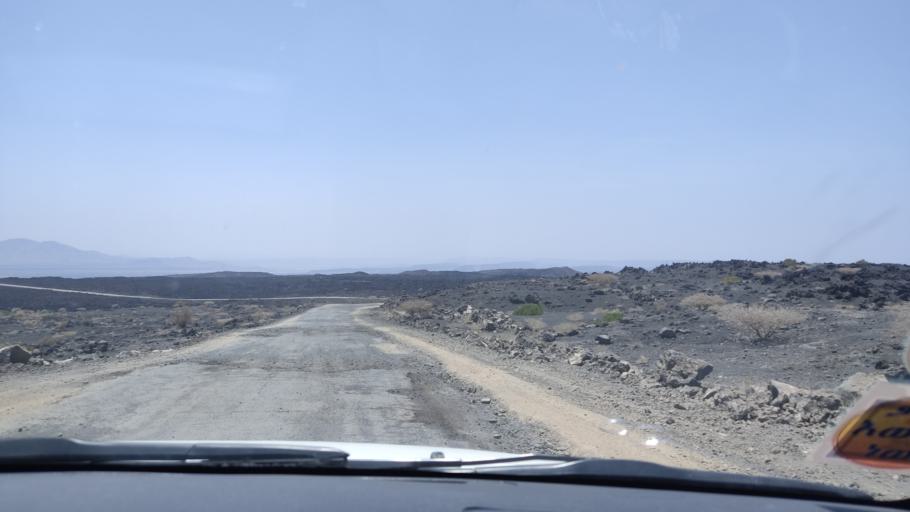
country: DJ
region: Tadjourah
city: Dorra
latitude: 12.3971
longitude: 42.1777
